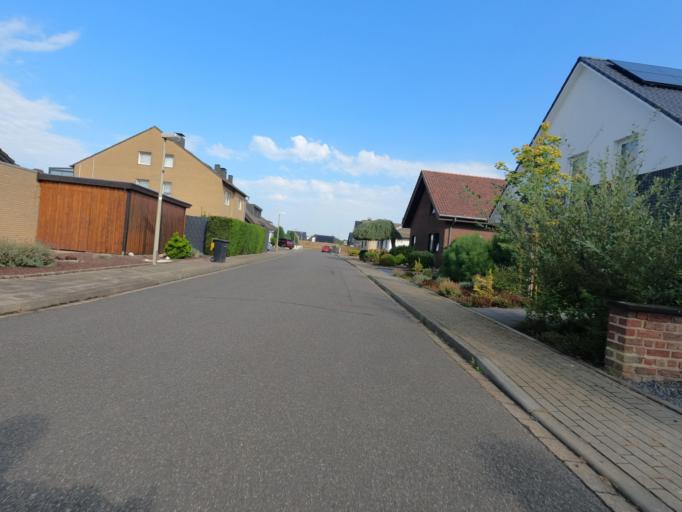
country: DE
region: North Rhine-Westphalia
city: Huckelhoven
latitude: 51.1000
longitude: 6.2378
